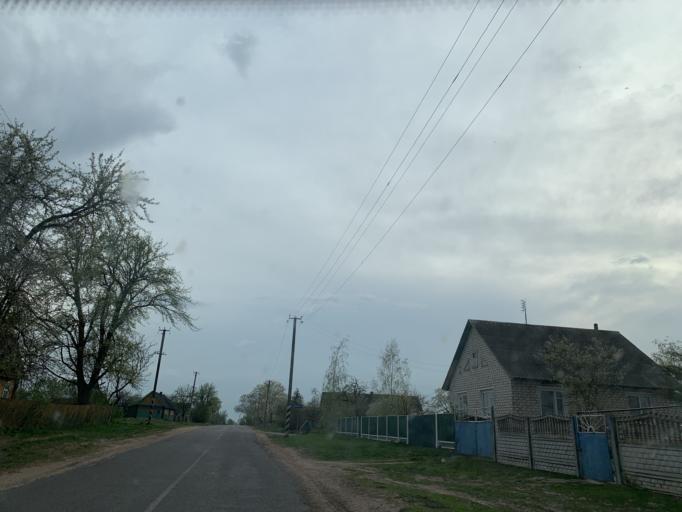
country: BY
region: Minsk
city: Kapyl'
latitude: 53.2845
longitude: 26.9829
